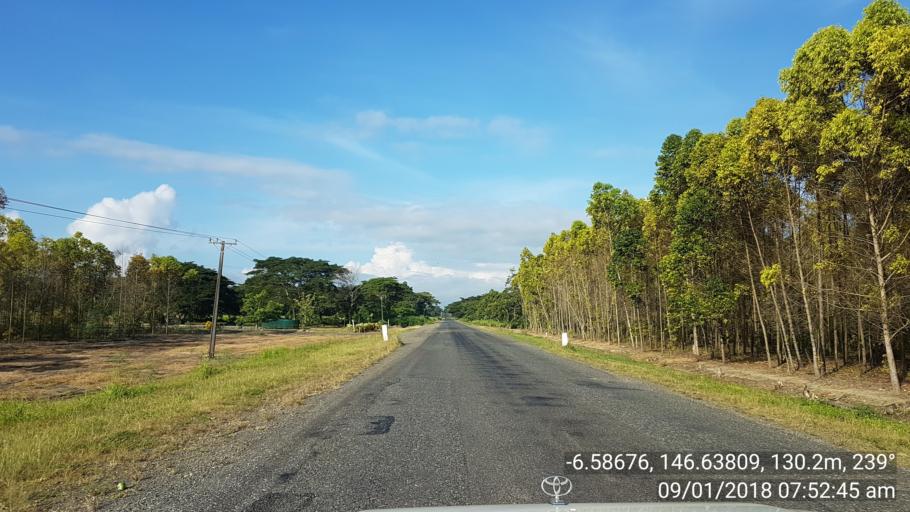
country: PG
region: Morobe
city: Lae
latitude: -6.5867
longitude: 146.6381
